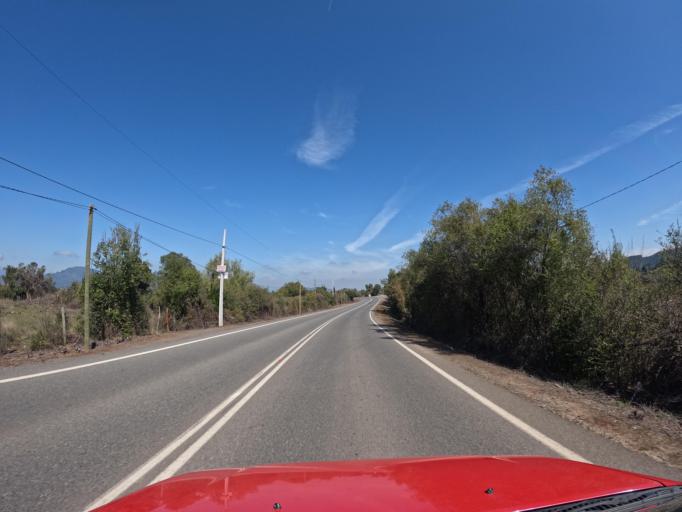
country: CL
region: Maule
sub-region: Provincia de Talca
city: San Clemente
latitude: -35.4473
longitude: -71.2693
